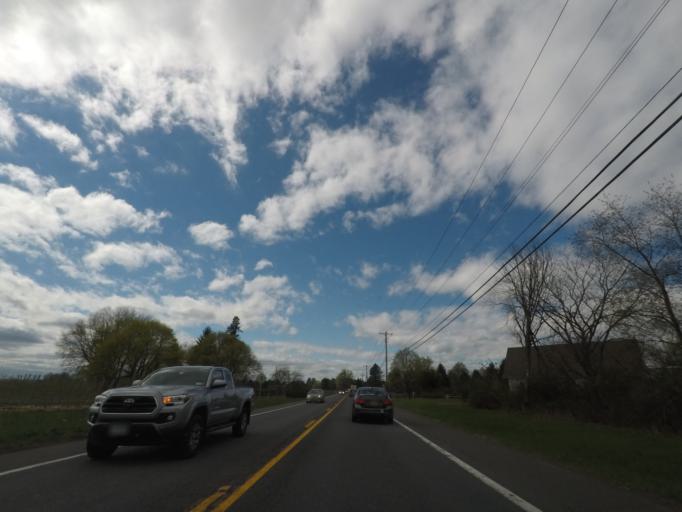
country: US
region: New York
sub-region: Columbia County
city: Niverville
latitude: 42.4480
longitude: -73.6895
